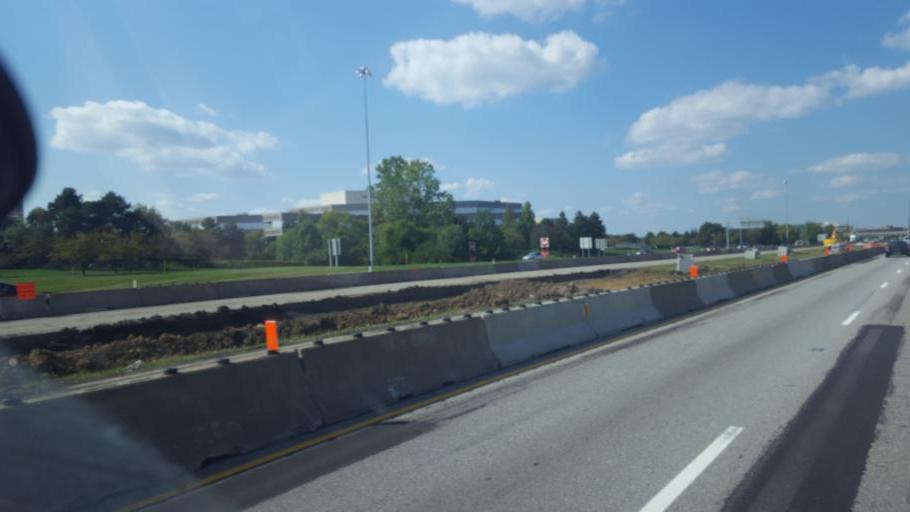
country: US
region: Ohio
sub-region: Franklin County
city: Dublin
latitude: 40.0773
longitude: -83.1358
